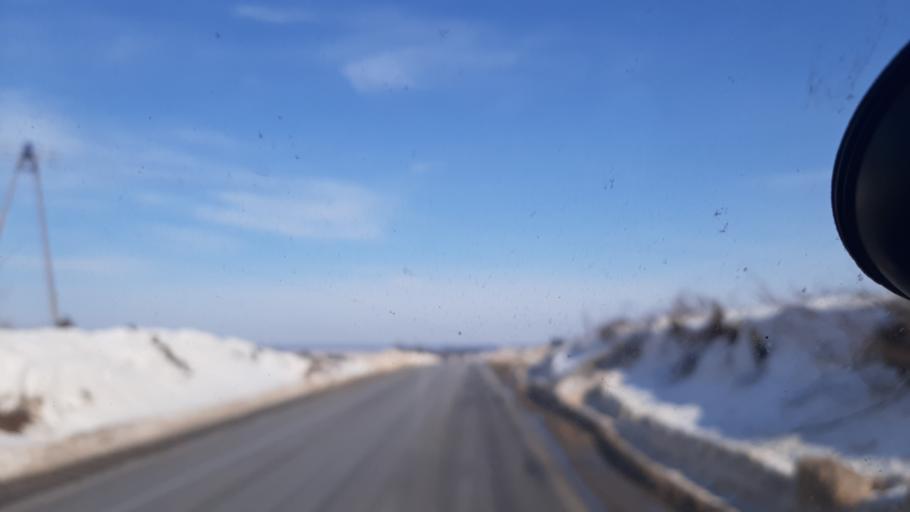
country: PL
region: Lublin Voivodeship
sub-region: Powiat pulawski
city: Kurow
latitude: 51.3660
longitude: 22.1435
